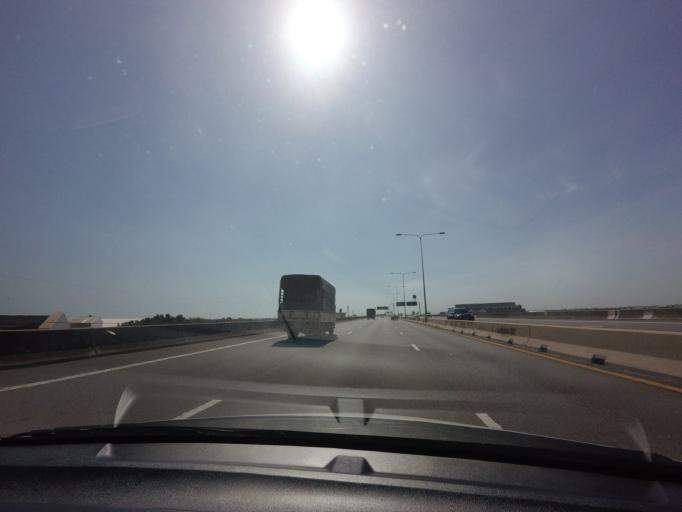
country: TH
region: Samut Prakan
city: Bang Bo
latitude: 13.5765
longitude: 100.8908
